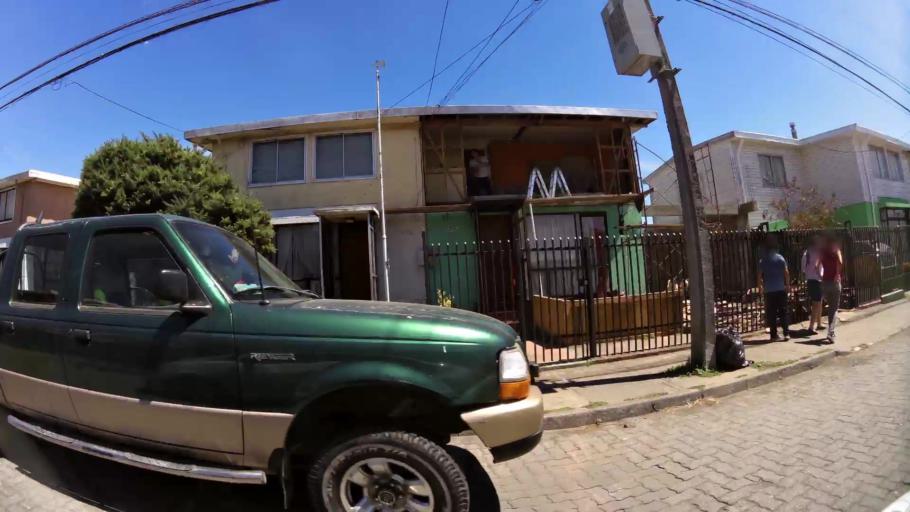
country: CL
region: Biobio
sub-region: Provincia de Concepcion
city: Talcahuano
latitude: -36.7563
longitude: -73.0898
